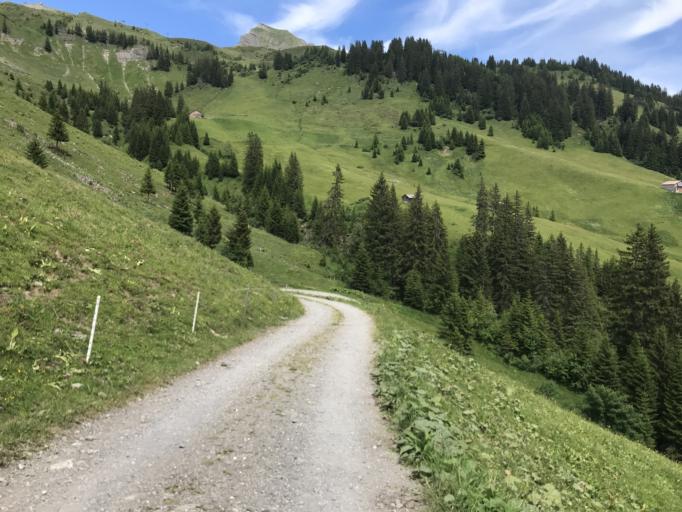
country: AT
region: Vorarlberg
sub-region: Politischer Bezirk Bregenz
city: Damuels
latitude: 47.2978
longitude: 9.8717
